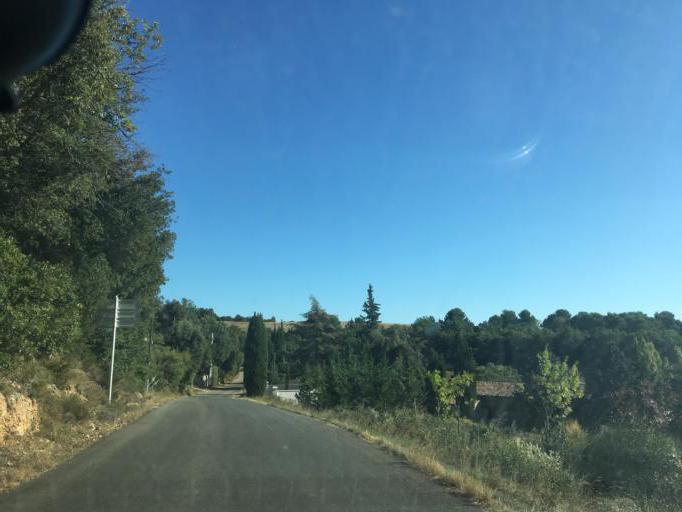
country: FR
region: Provence-Alpes-Cote d'Azur
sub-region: Departement du Var
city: Regusse
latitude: 43.7115
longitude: 6.1421
